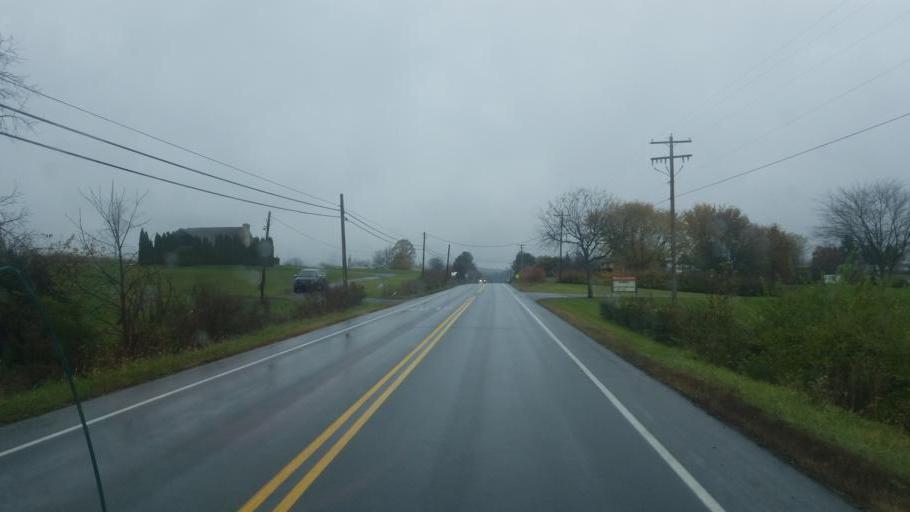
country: US
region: Pennsylvania
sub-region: Clinton County
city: Mill Hall
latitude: 41.0678
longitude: -77.6007
